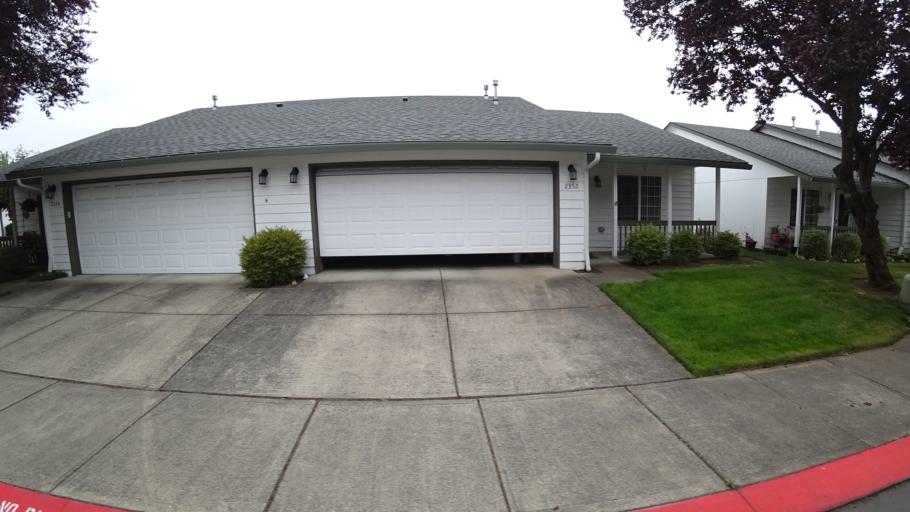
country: US
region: Oregon
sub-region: Washington County
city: Aloha
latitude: 45.5018
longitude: -122.9199
